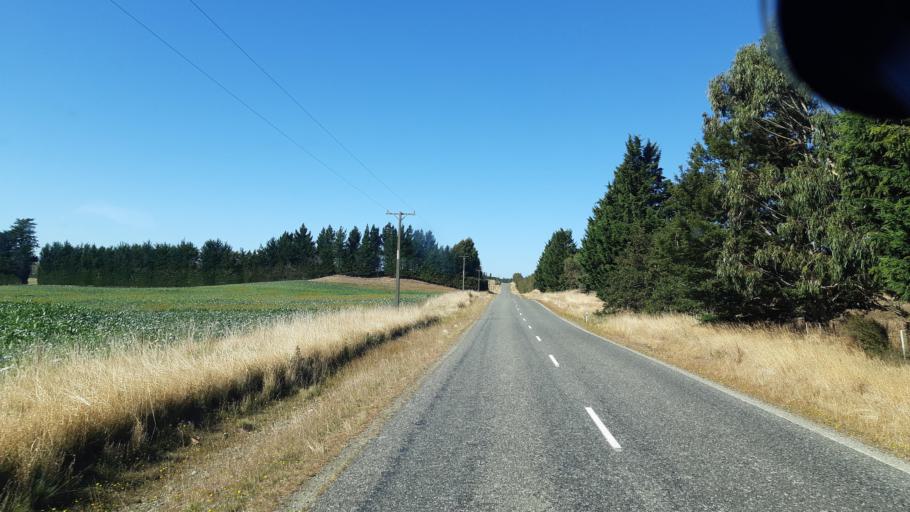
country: NZ
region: Southland
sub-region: Gore District
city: Gore
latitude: -45.9663
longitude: 168.7018
